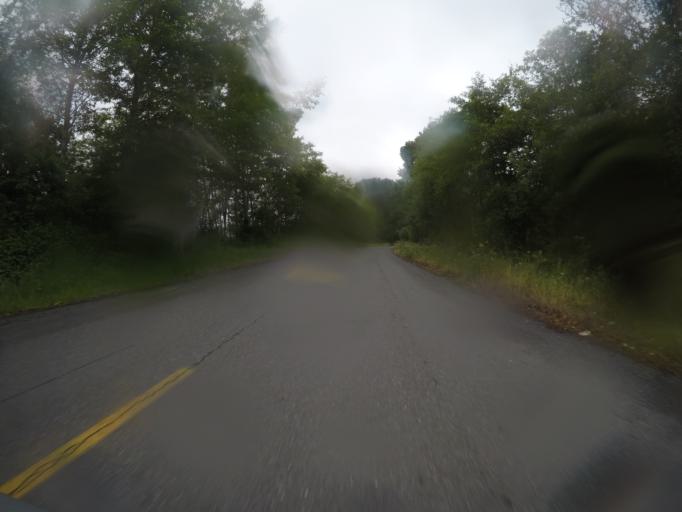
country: US
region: California
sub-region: Humboldt County
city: Westhaven-Moonstone
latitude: 41.3001
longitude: -124.0434
